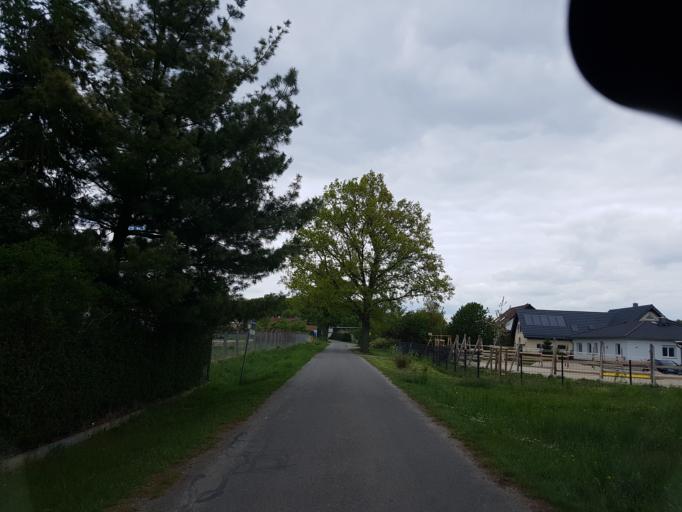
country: DE
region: Brandenburg
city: Bronkow
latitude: 51.6045
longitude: 13.9094
